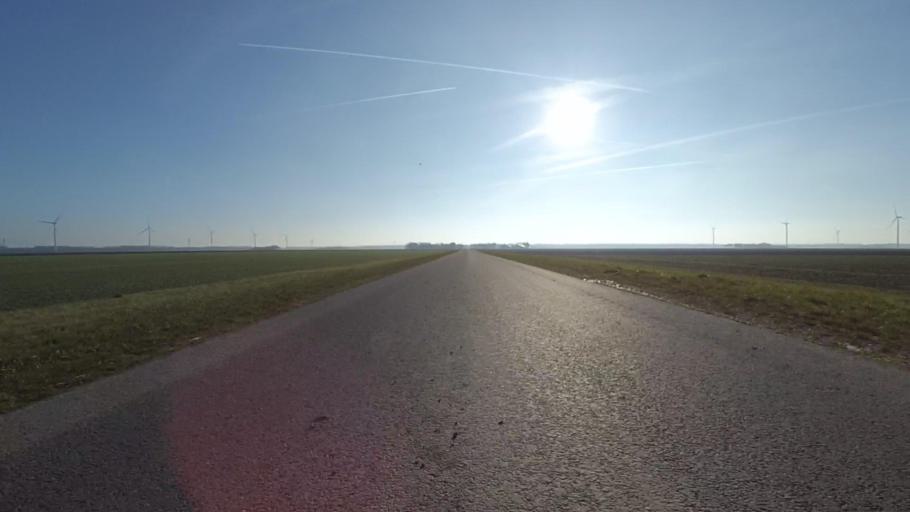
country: NL
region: Utrecht
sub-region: Gemeente Bunschoten
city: Bunschoten
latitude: 52.3010
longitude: 5.4229
